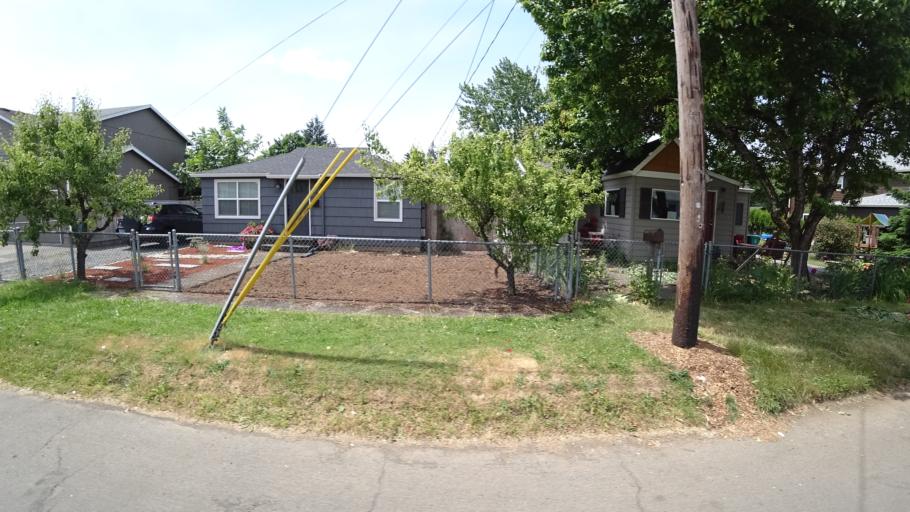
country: US
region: Oregon
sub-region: Multnomah County
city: Lents
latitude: 45.4692
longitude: -122.5972
